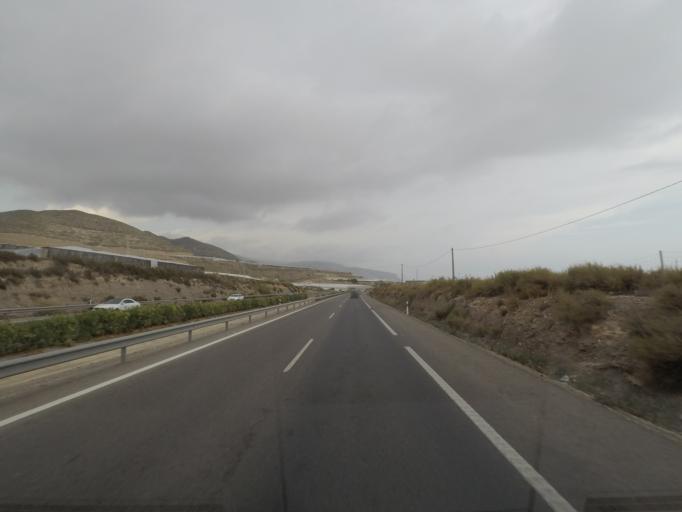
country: ES
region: Andalusia
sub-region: Provincia de Almeria
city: Vicar
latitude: 36.8116
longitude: -2.6281
